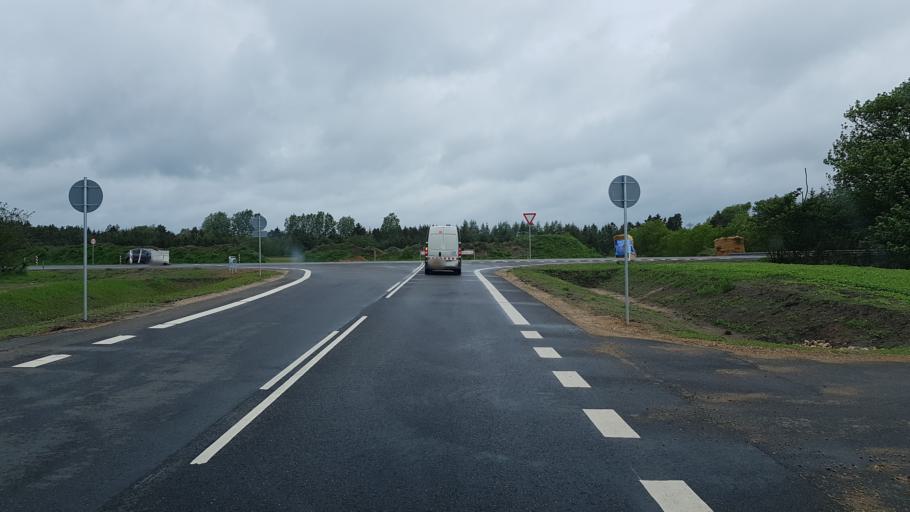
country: DK
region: Central Jutland
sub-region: Skive Kommune
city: Skive
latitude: 56.4029
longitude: 8.9732
